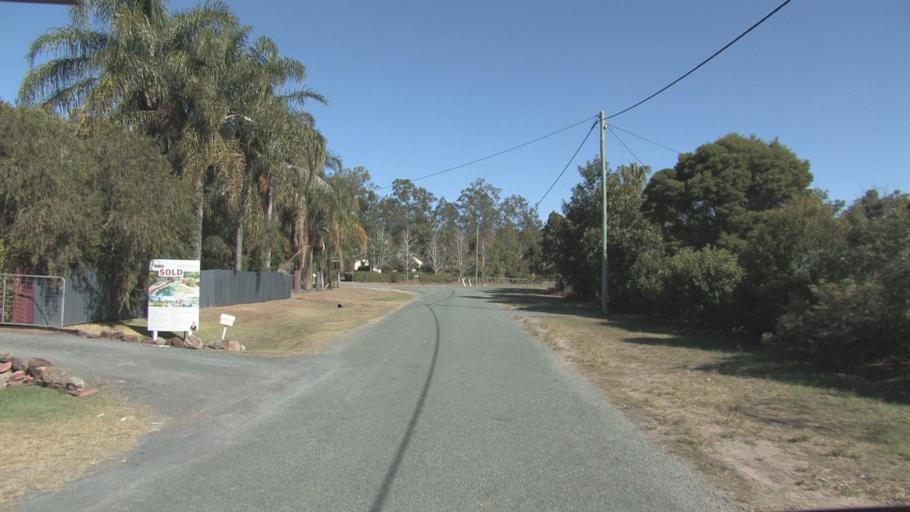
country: AU
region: Queensland
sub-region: Logan
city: Cedar Vale
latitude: -27.8499
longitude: 153.0190
